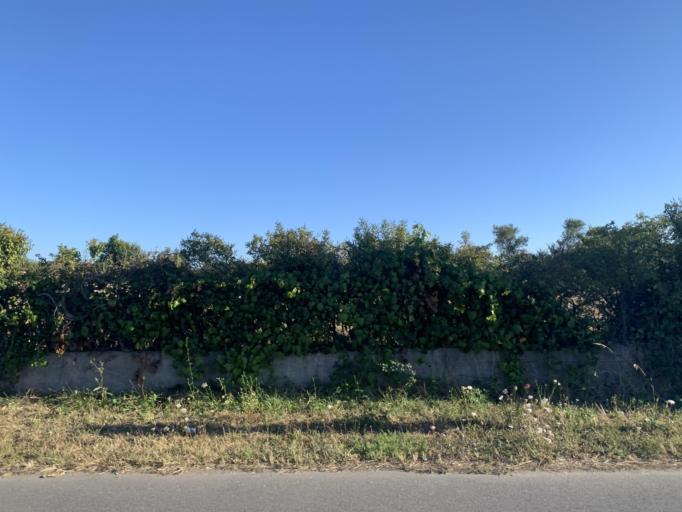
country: FR
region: Pays de la Loire
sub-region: Departement de la Loire-Atlantique
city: Pornichet
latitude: 47.2588
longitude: -2.2770
